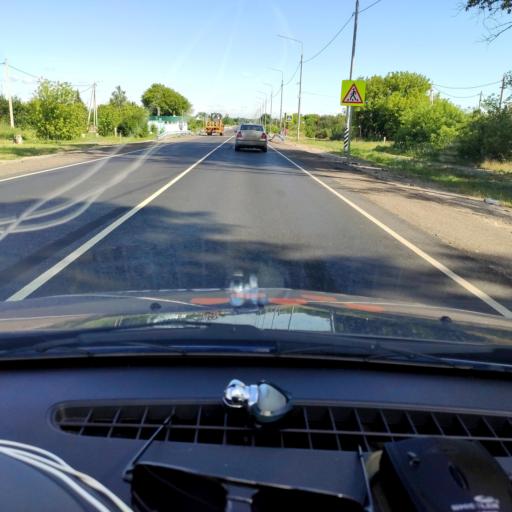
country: RU
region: Lipetsk
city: Khlevnoye
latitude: 52.1201
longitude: 39.1664
